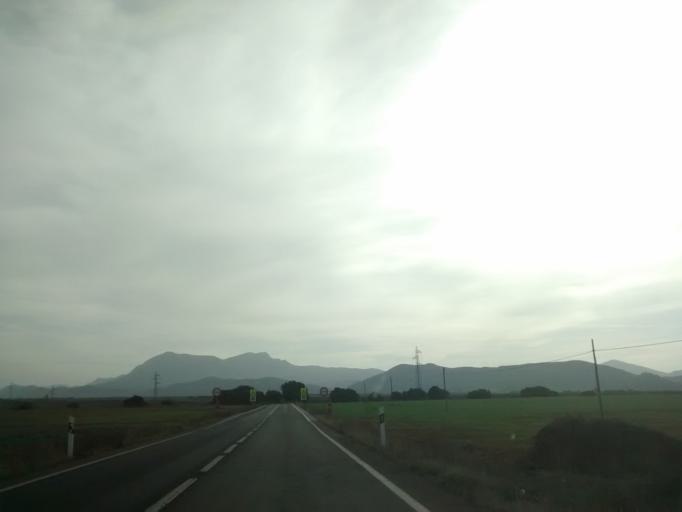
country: ES
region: Aragon
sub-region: Provincia de Huesca
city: Bailo
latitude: 42.5909
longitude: -0.8411
